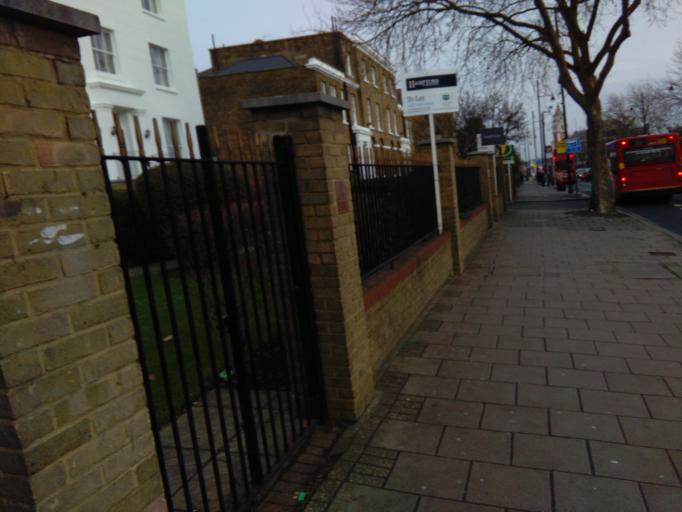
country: GB
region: England
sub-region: Greater London
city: Brixton Hill
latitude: 51.4602
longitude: -0.1207
